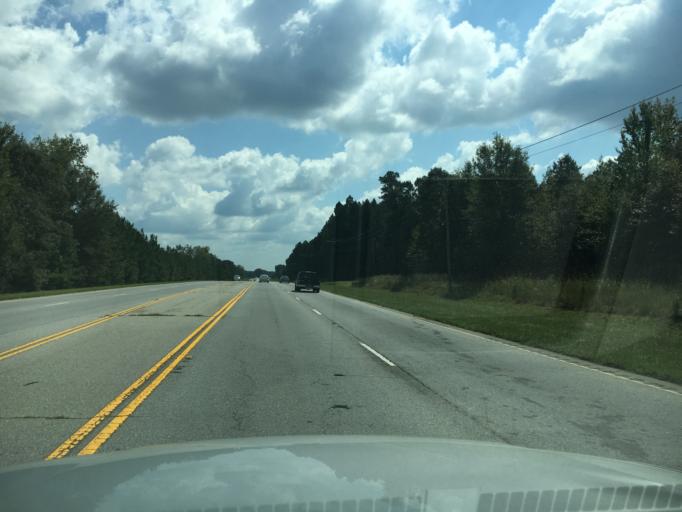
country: US
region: South Carolina
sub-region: Anderson County
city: Williamston
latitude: 34.6015
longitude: -82.3571
